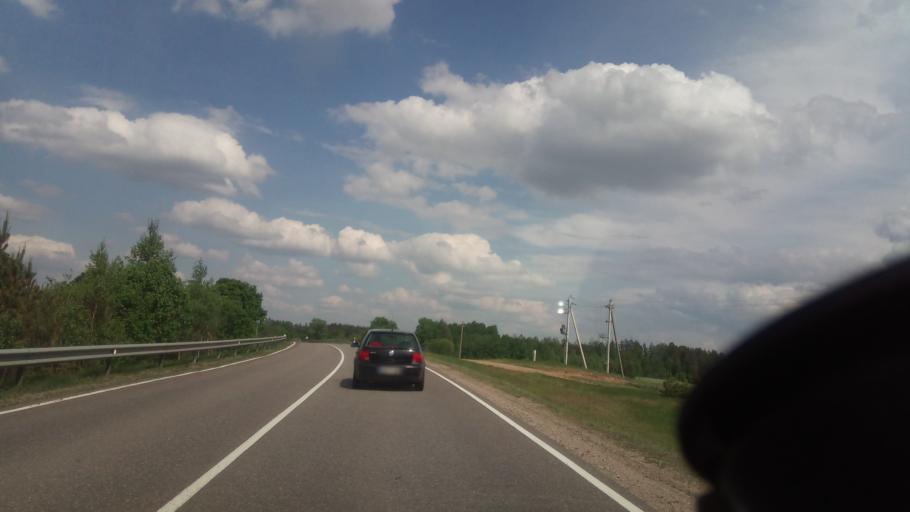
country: LT
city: Trakai
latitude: 54.6097
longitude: 24.8702
